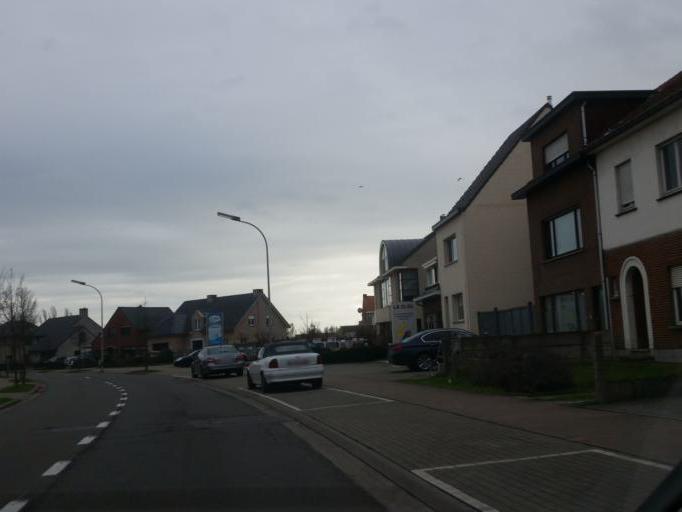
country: BE
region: Flanders
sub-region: Provincie Antwerpen
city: Duffel
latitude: 51.0694
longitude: 4.4877
